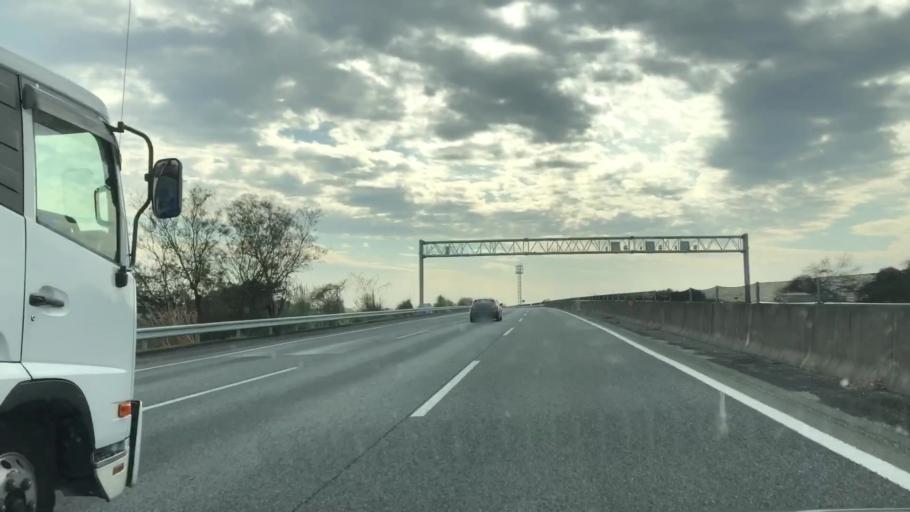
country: JP
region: Saga Prefecture
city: Tosu
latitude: 33.3572
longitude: 130.5391
